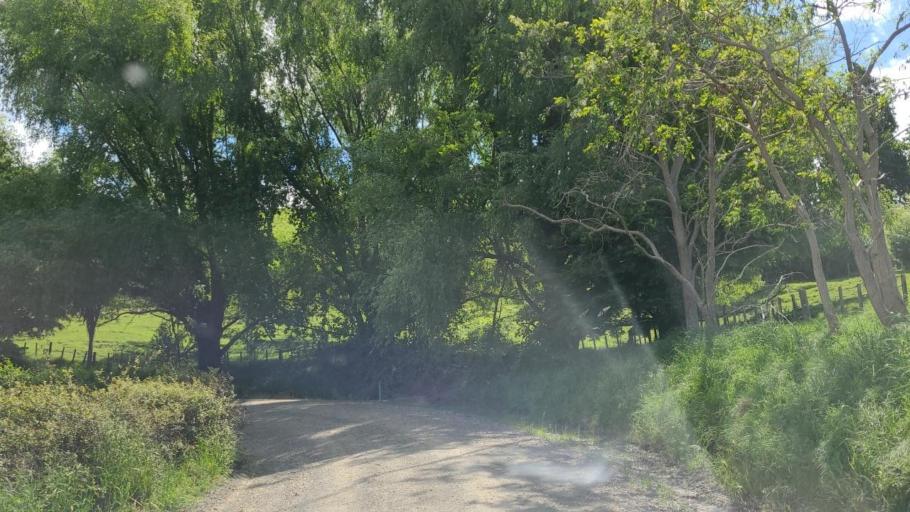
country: NZ
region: Hawke's Bay
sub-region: Napier City
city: Napier
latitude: -39.3694
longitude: 176.7928
